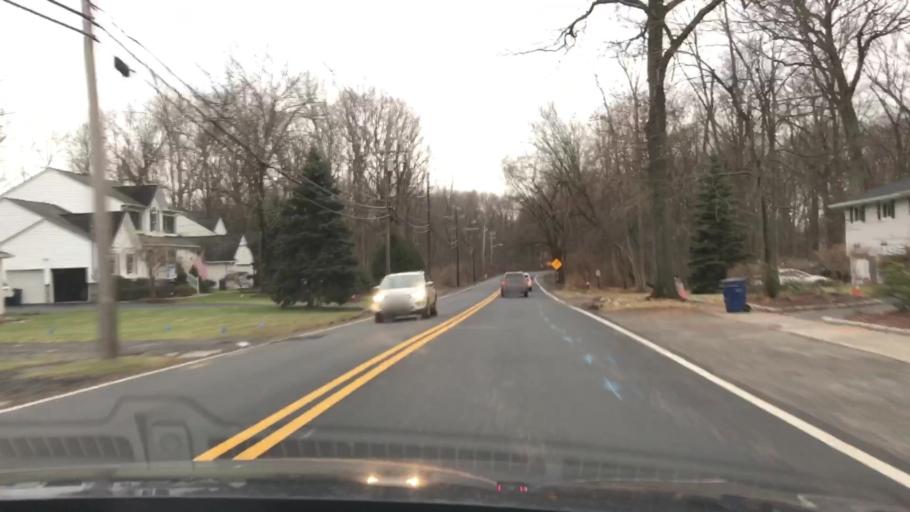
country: US
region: New Jersey
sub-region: Bergen County
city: Norwood
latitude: 40.9893
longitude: -73.9581
